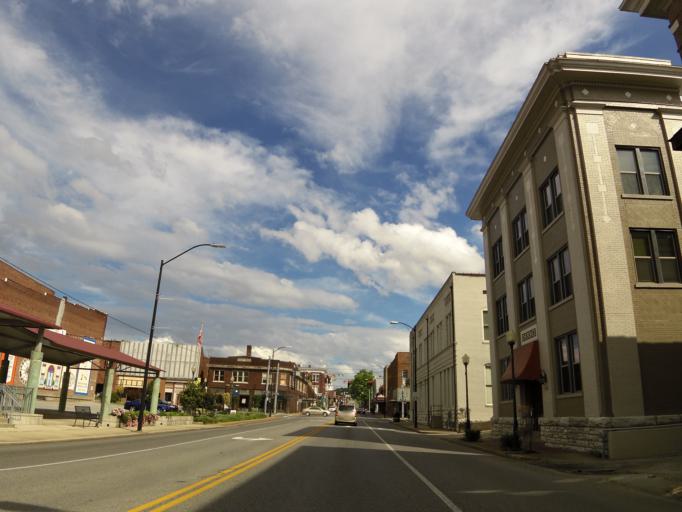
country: US
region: Kentucky
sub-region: Christian County
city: Hopkinsville
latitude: 36.8659
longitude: -87.4897
